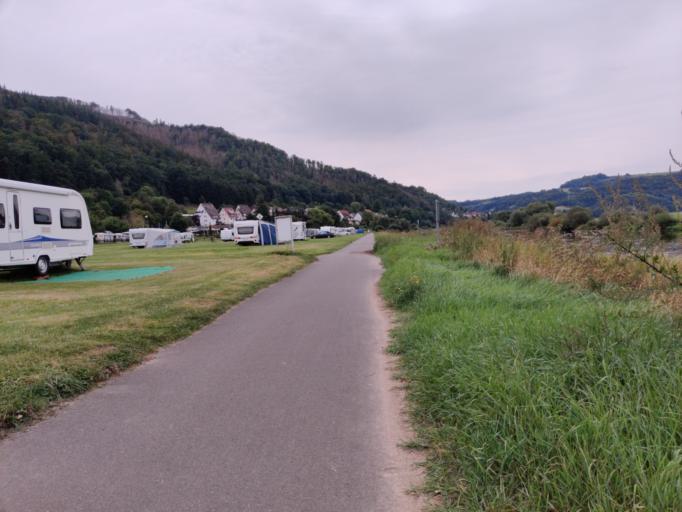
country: DE
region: Lower Saxony
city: Pegestorf
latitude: 51.9419
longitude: 9.5090
